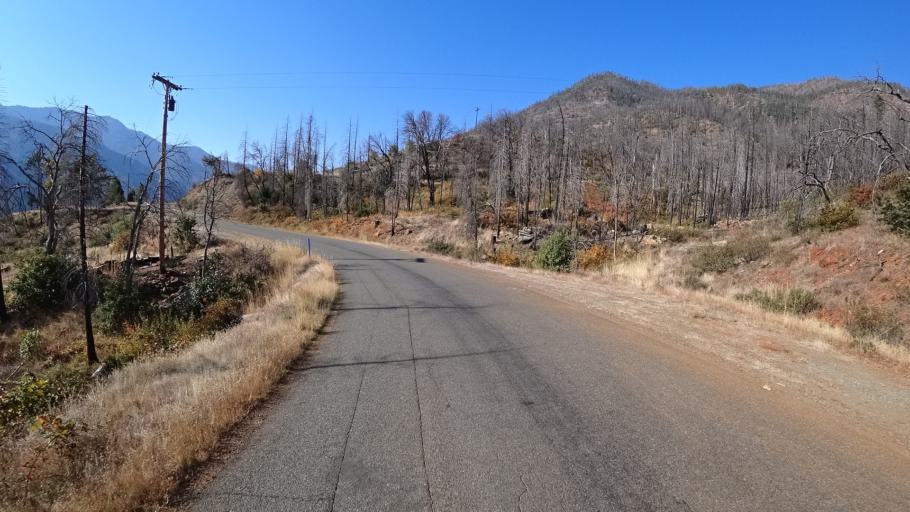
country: US
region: California
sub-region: Siskiyou County
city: Happy Camp
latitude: 41.7268
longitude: -123.0140
